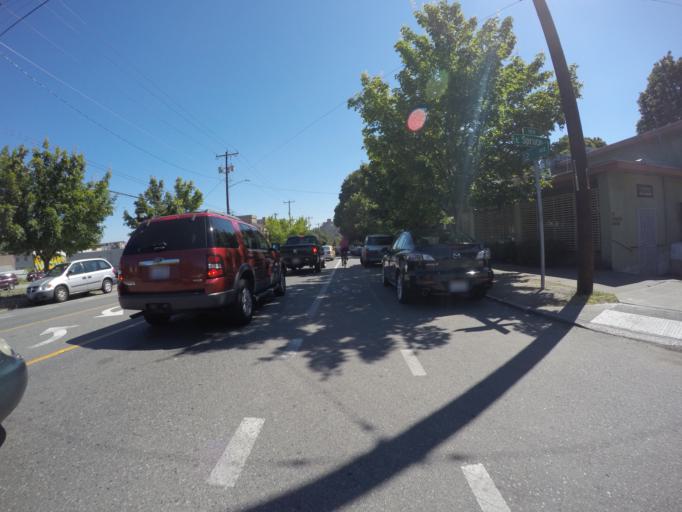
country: US
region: Washington
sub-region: King County
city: Seattle
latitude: 47.6034
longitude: -122.3169
